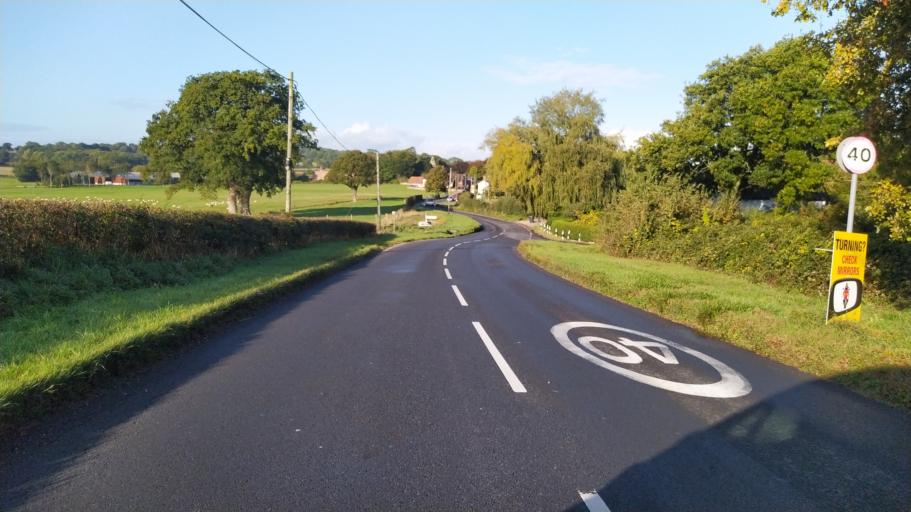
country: GB
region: England
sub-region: Dorset
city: Three Legged Cross
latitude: 50.8667
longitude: -1.9521
